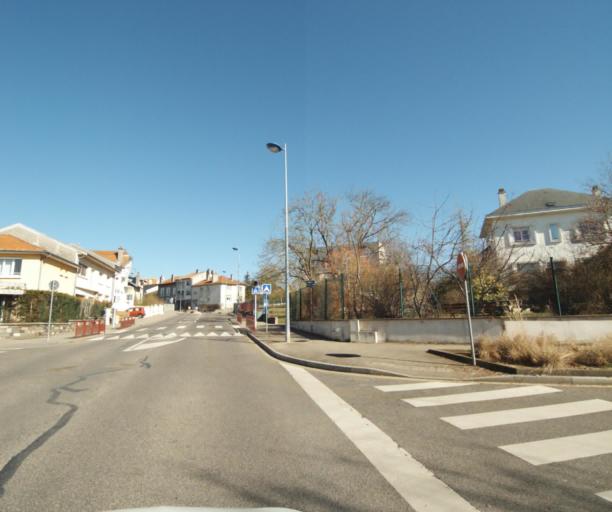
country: FR
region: Lorraine
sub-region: Departement de Meurthe-et-Moselle
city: Saint-Max
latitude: 48.7059
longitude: 6.2034
